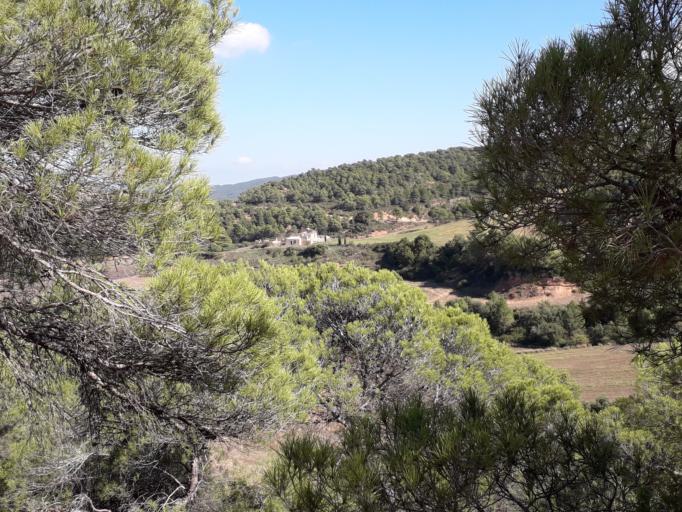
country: ES
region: Catalonia
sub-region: Provincia de Barcelona
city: Sant Marti de Tous
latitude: 41.5349
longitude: 1.4779
